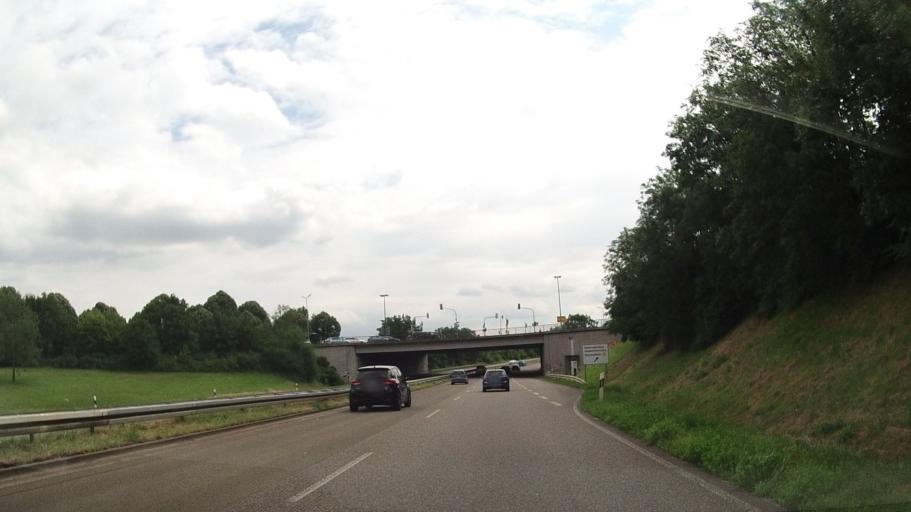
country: DE
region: Baden-Wuerttemberg
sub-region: Karlsruhe Region
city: Rheinstetten
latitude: 48.9958
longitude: 8.3429
